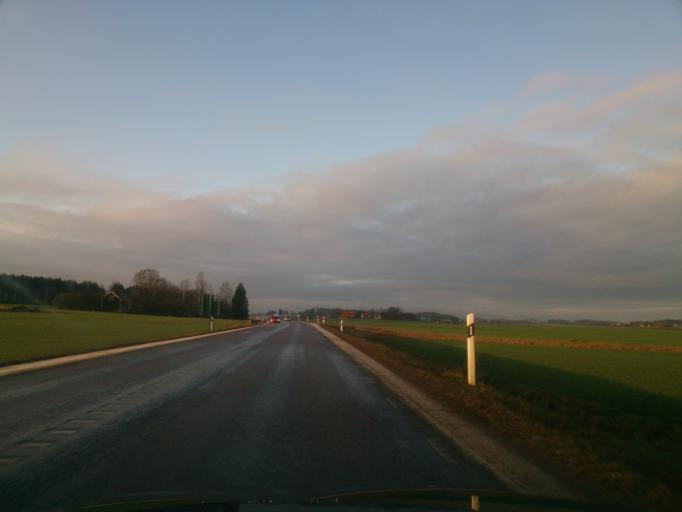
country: SE
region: OEstergoetland
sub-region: Linkopings Kommun
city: Linghem
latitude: 58.4010
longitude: 15.7477
